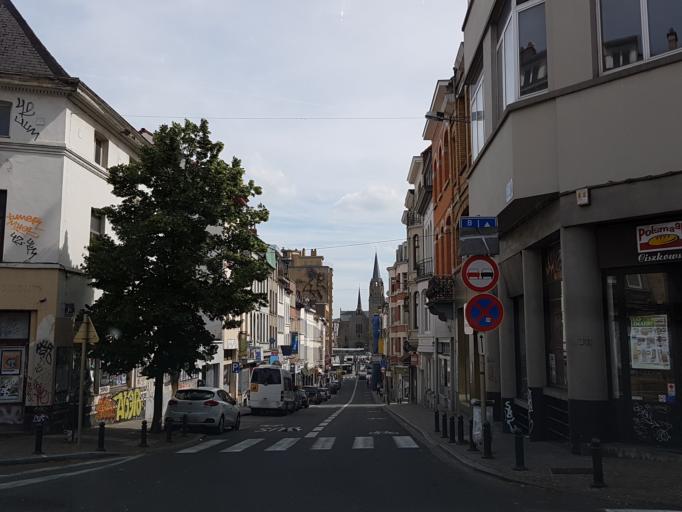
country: BE
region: Brussels Capital
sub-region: Bruxelles-Capitale
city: Brussels
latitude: 50.8297
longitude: 4.3699
